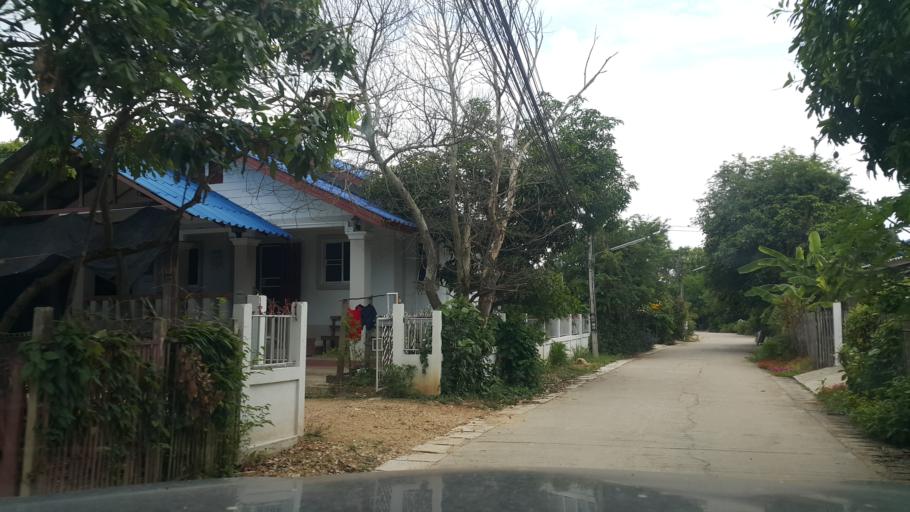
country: TH
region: Lamphun
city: Ban Thi
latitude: 18.6709
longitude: 99.1501
